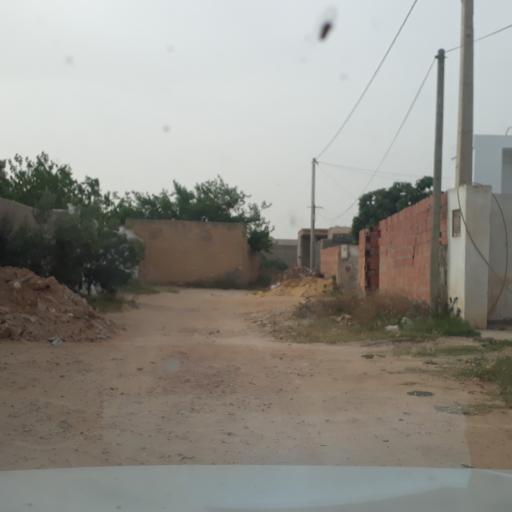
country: TN
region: Safaqis
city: Al Qarmadah
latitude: 34.8209
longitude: 10.7737
